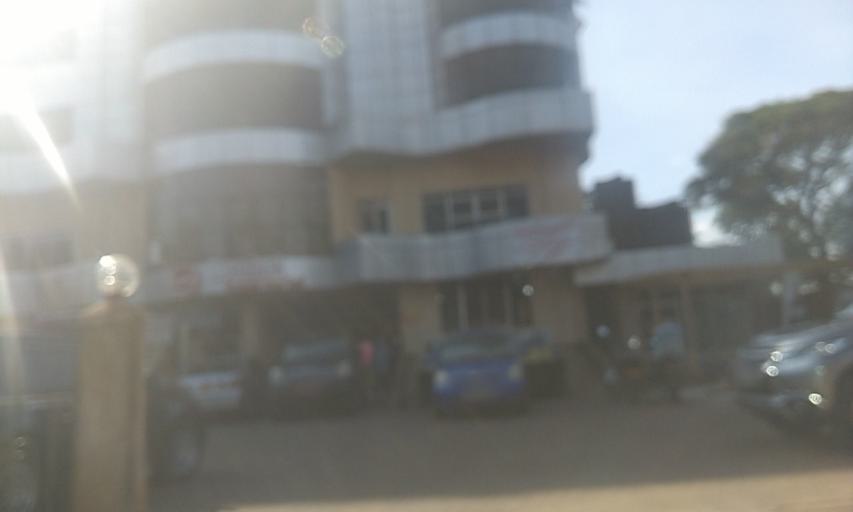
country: UG
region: Central Region
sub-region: Wakiso District
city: Kireka
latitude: 0.3636
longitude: 32.6259
